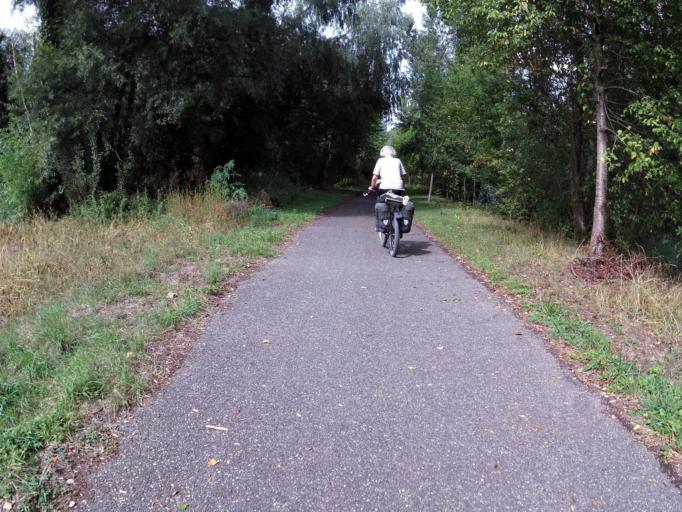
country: FR
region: Alsace
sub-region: Departement du Haut-Rhin
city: Biesheim
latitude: 48.0516
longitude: 7.5510
